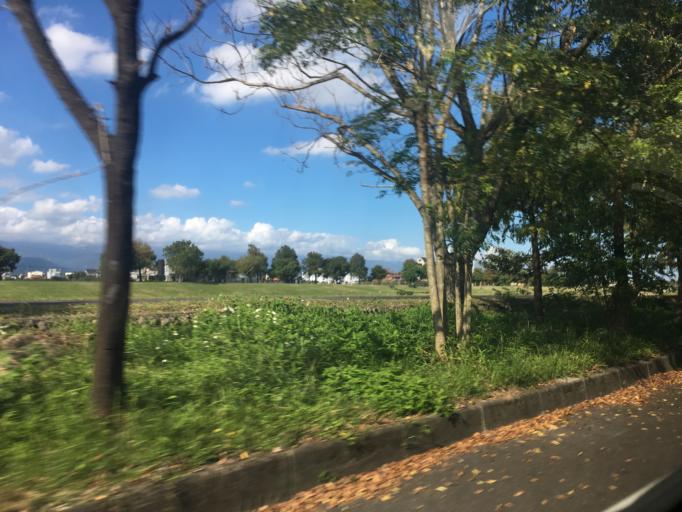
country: TW
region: Taiwan
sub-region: Yilan
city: Yilan
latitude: 24.6934
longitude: 121.7426
